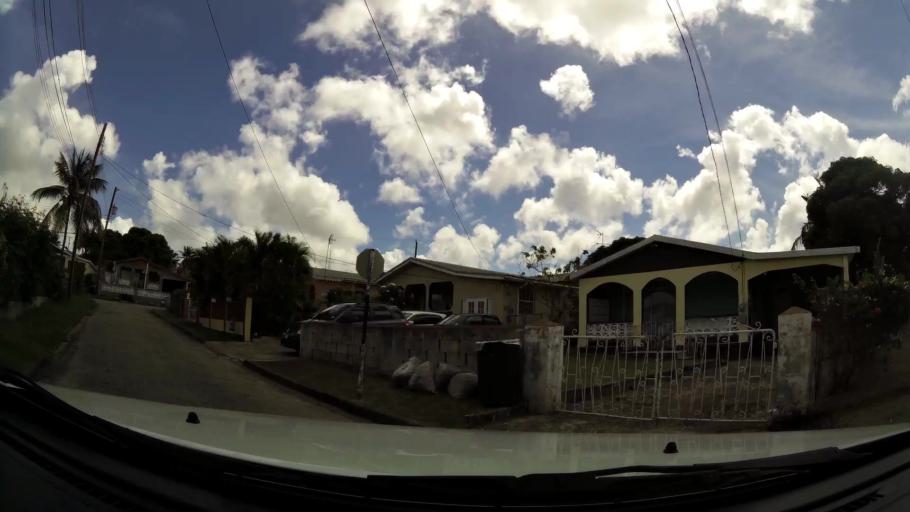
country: BB
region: Saint James
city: Holetown
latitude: 13.1524
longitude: -59.6283
